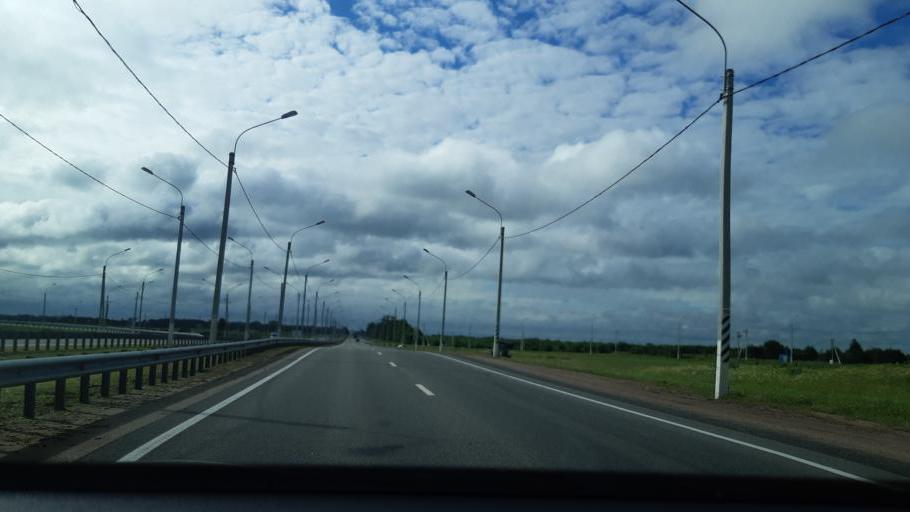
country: RU
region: Smolensk
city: Talashkino
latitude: 54.7040
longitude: 32.1191
